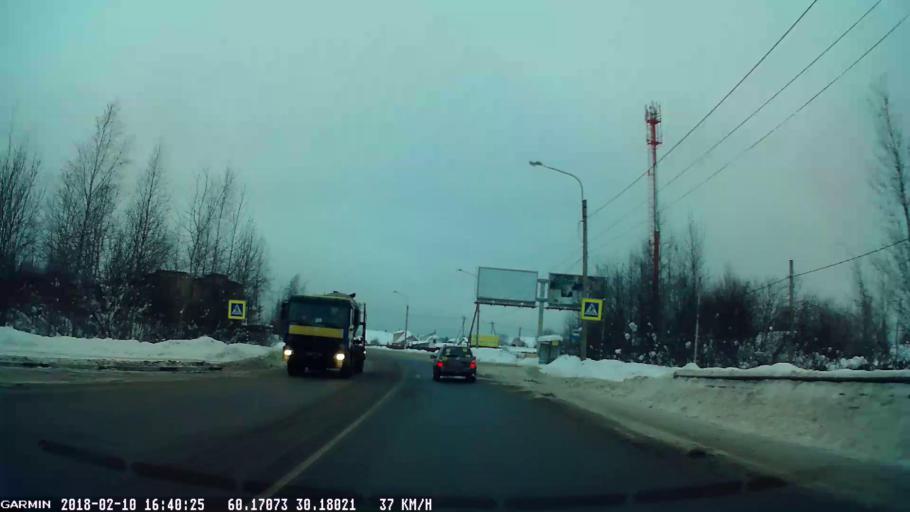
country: RU
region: Leningrad
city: Sertolovo
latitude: 60.1606
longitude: 30.1849
